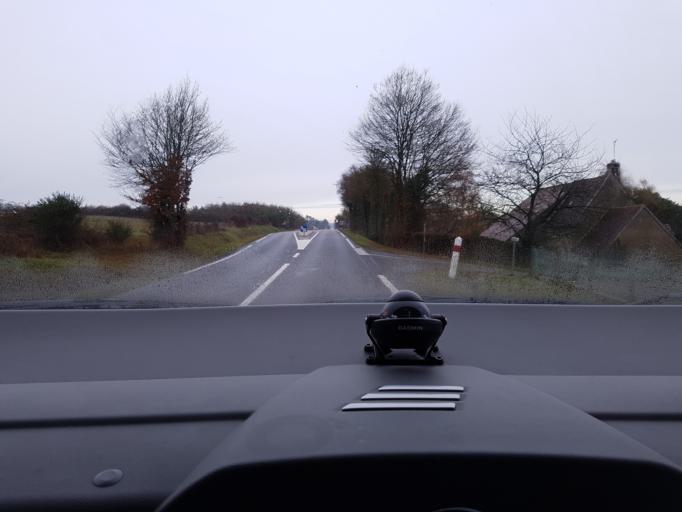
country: FR
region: Lower Normandy
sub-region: Departement de l'Orne
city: Saint-Sulpice-sur-Risle
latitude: 48.7735
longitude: 0.6416
